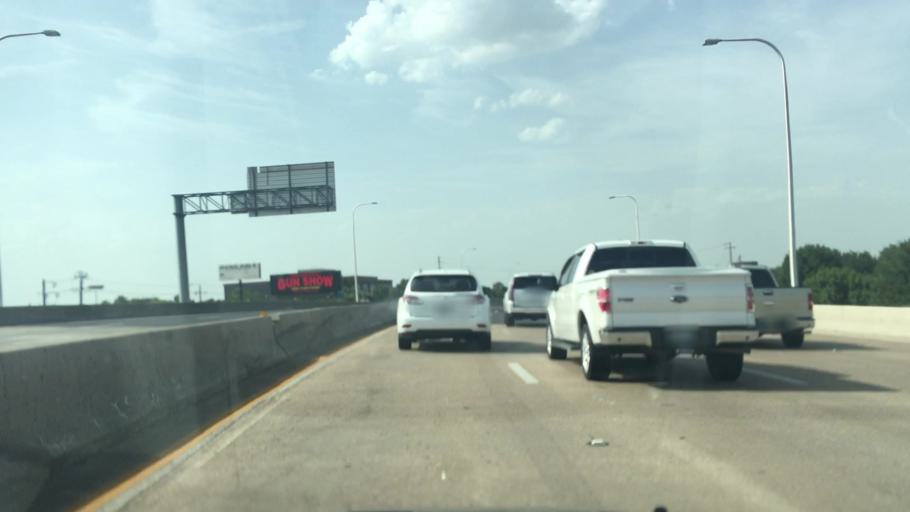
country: US
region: Texas
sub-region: Dallas County
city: Addison
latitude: 32.9904
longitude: -96.8292
